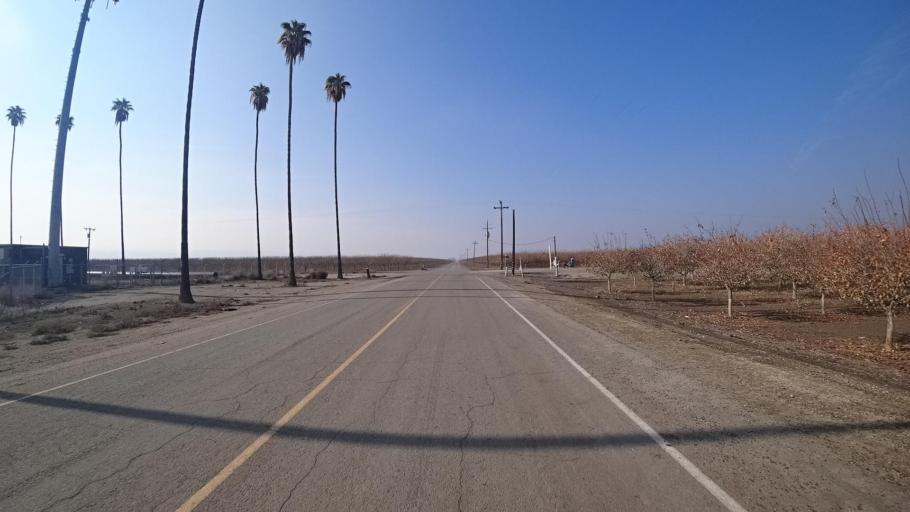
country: US
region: California
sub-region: Kern County
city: Buttonwillow
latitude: 35.3403
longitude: -119.3939
